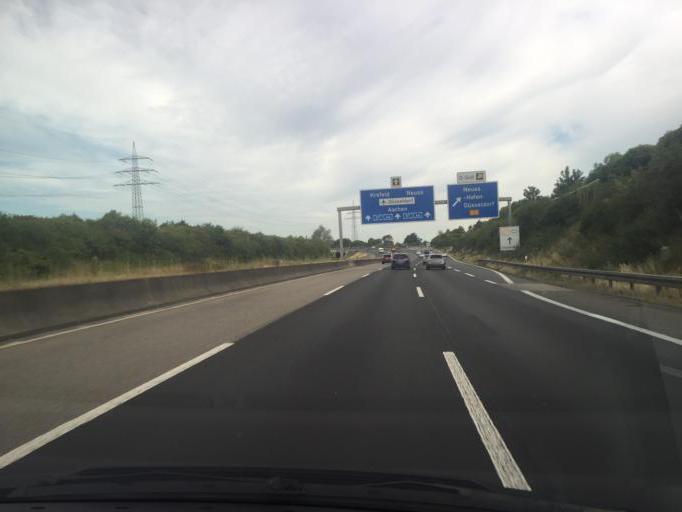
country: DE
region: North Rhine-Westphalia
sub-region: Regierungsbezirk Dusseldorf
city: Neuss
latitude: 51.1752
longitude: 6.7139
